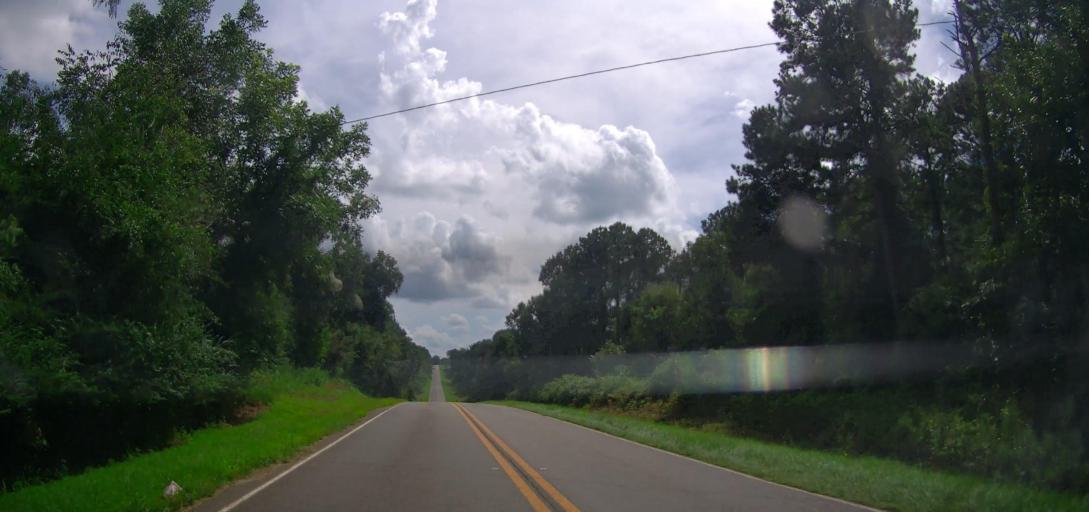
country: US
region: Georgia
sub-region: Taylor County
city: Butler
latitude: 32.4871
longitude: -84.2057
